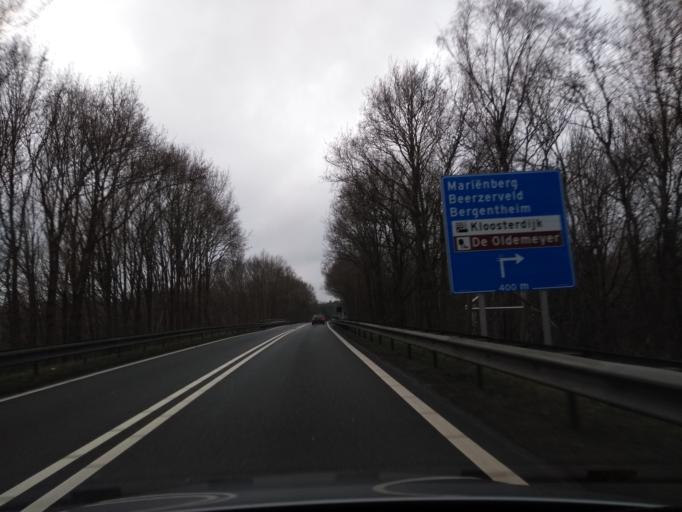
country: NL
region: Overijssel
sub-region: Gemeente Twenterand
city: Vroomshoop
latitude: 52.5058
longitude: 6.5673
